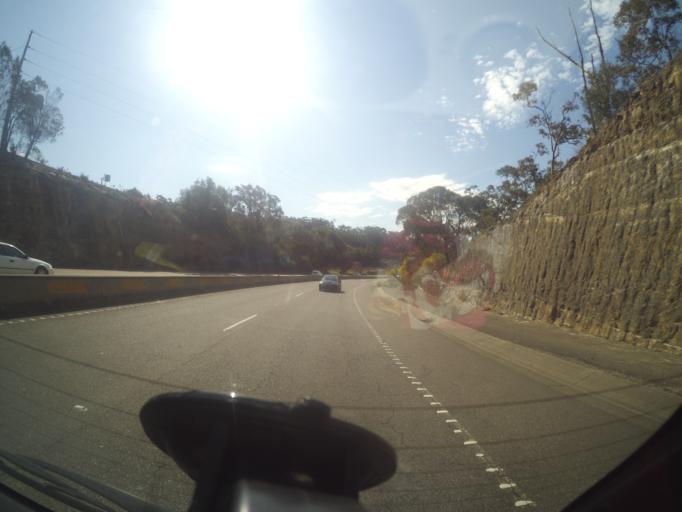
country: AU
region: New South Wales
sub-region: Blue Mountains Municipality
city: Hazelbrook
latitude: -33.7212
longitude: 150.4944
